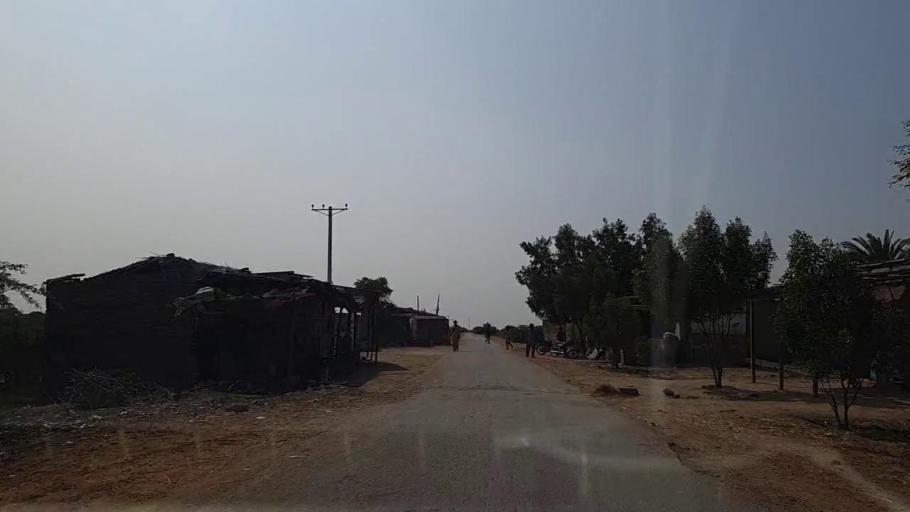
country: PK
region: Sindh
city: Chuhar Jamali
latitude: 24.3054
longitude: 67.9360
